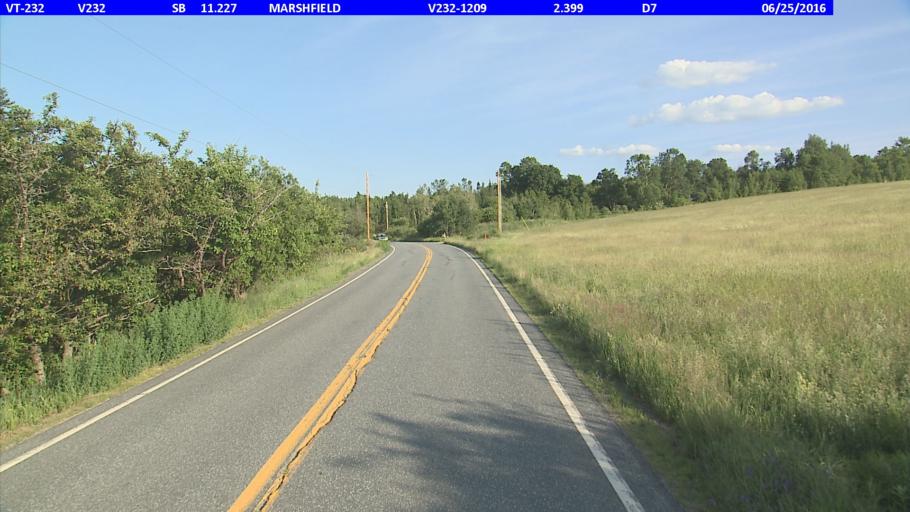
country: US
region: Vermont
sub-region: Caledonia County
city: Hardwick
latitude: 44.3419
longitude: -72.2951
